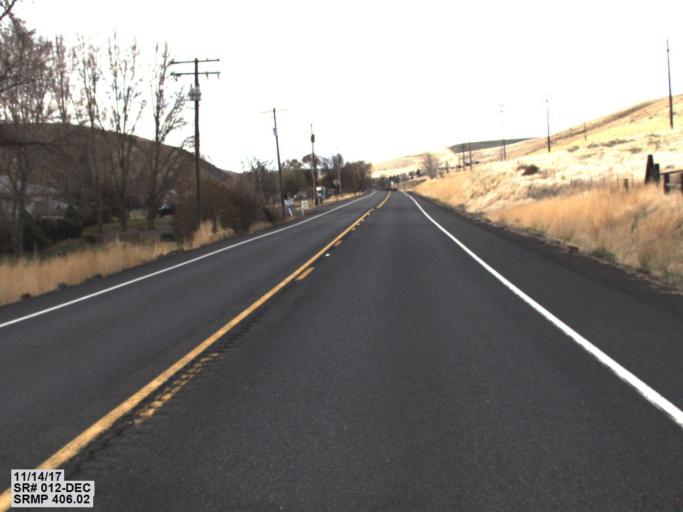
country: US
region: Washington
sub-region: Garfield County
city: Pomeroy
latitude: 46.4743
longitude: -117.5469
